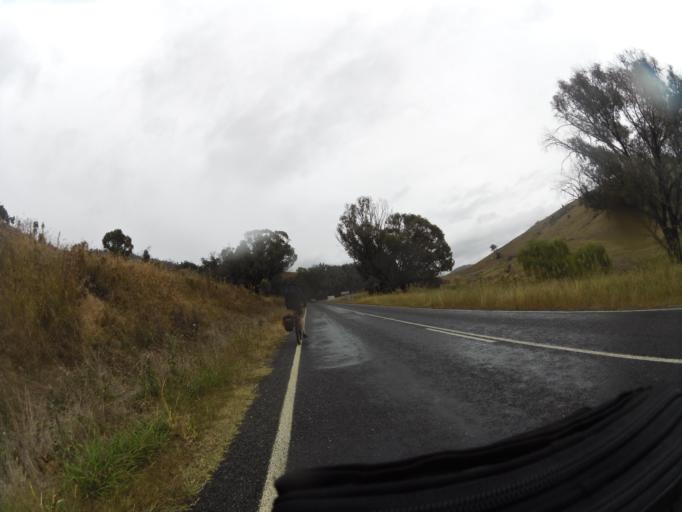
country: AU
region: New South Wales
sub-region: Greater Hume Shire
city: Holbrook
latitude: -36.2219
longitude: 147.7291
